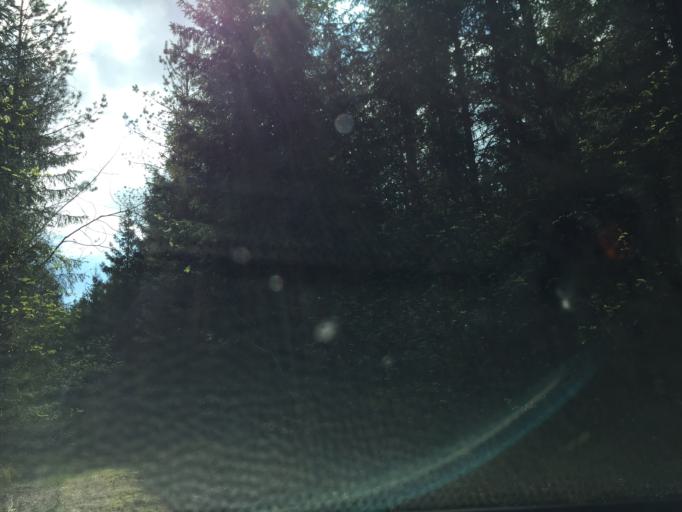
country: LV
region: Sigulda
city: Sigulda
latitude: 57.3220
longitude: 24.8582
